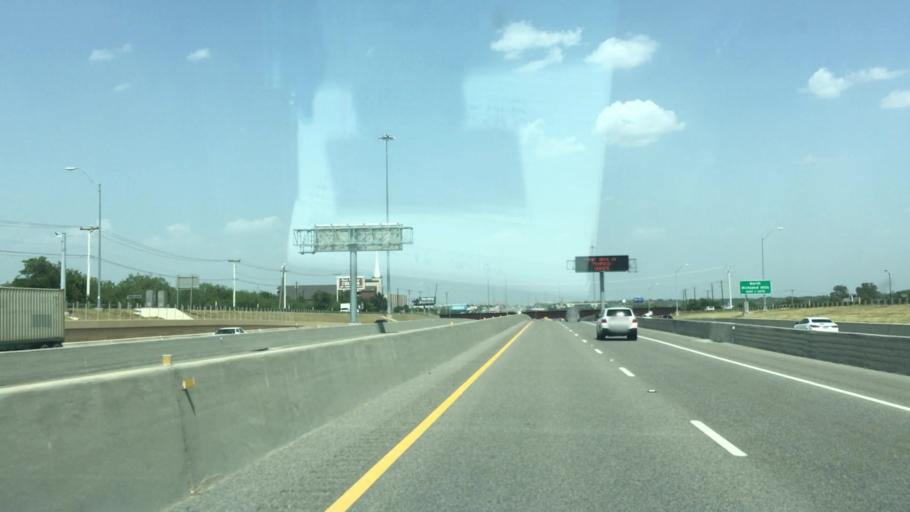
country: US
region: Texas
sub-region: Tarrant County
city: Watauga
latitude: 32.8393
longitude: -97.2753
